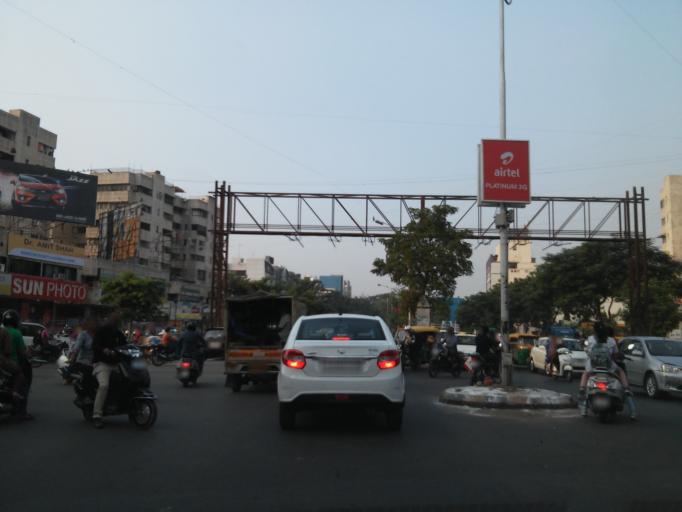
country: IN
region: Gujarat
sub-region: Ahmadabad
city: Sarkhej
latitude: 23.0159
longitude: 72.5304
